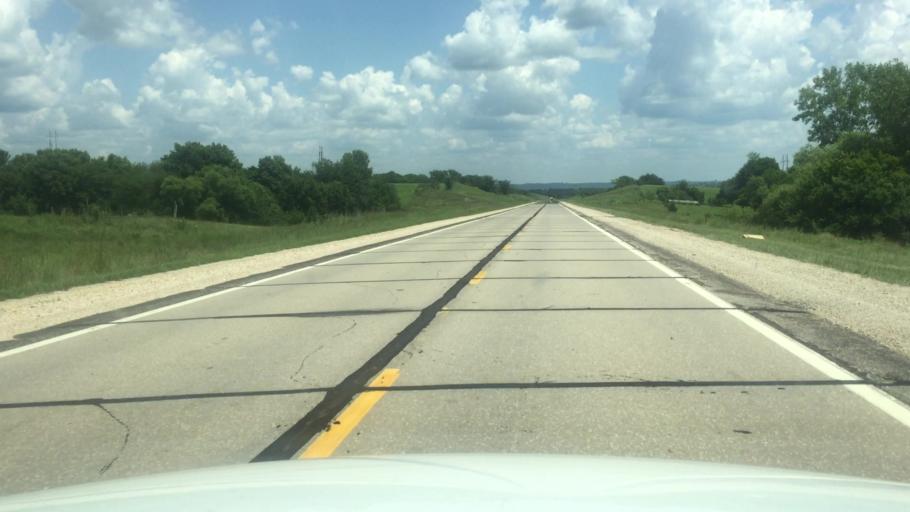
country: US
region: Kansas
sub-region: Atchison County
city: Atchison
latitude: 39.5571
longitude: -95.1812
